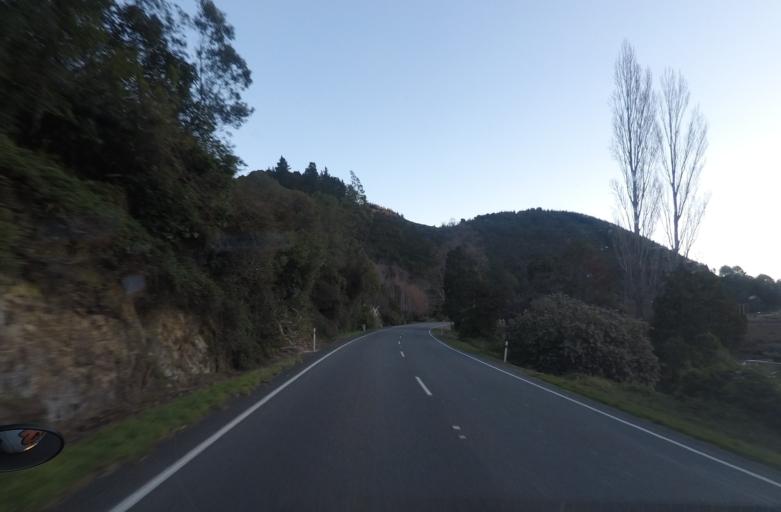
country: NZ
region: Marlborough
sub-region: Marlborough District
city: Picton
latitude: -41.2743
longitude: 173.7439
